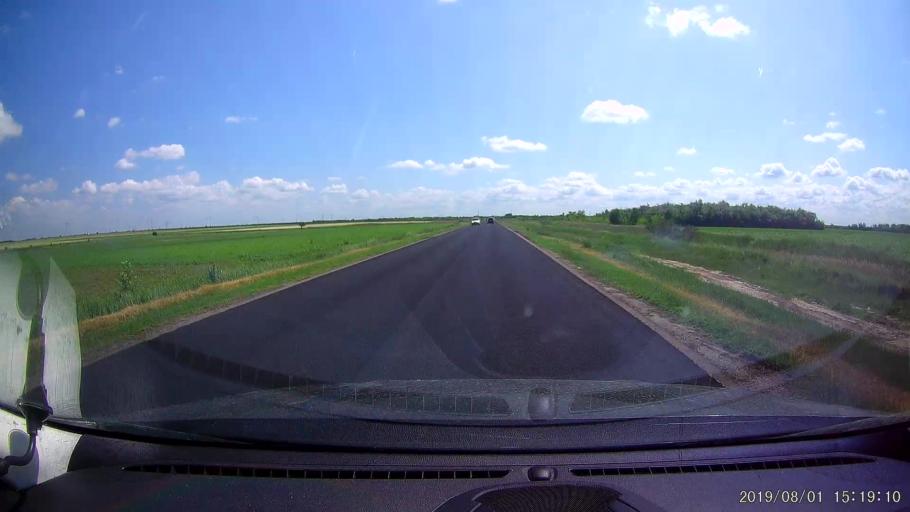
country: RO
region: Braila
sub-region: Comuna Unirea
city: Unirea
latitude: 45.0938
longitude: 27.8147
